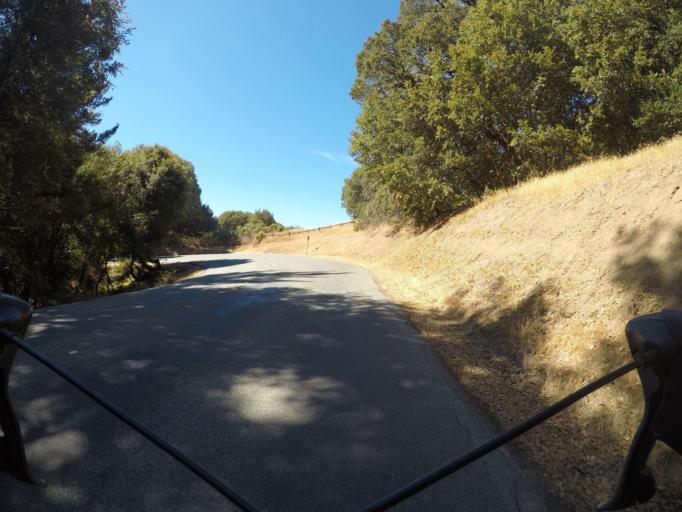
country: US
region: California
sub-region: San Mateo County
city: Portola Valley
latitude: 37.3147
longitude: -122.1969
